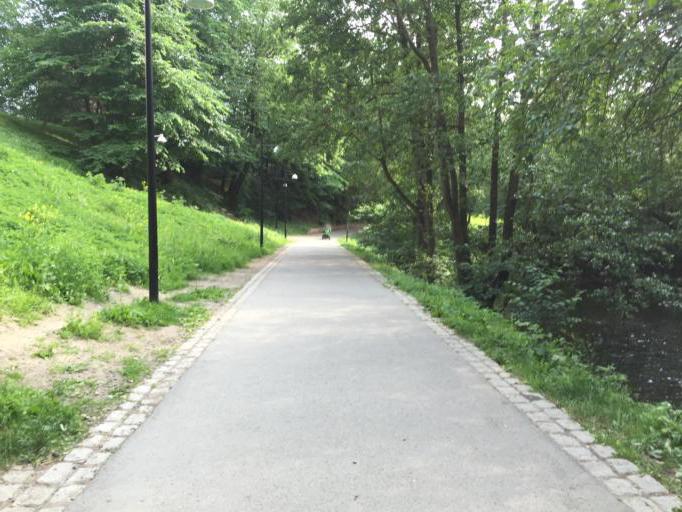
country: NO
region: Oslo
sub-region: Oslo
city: Oslo
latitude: 59.9279
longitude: 10.7553
